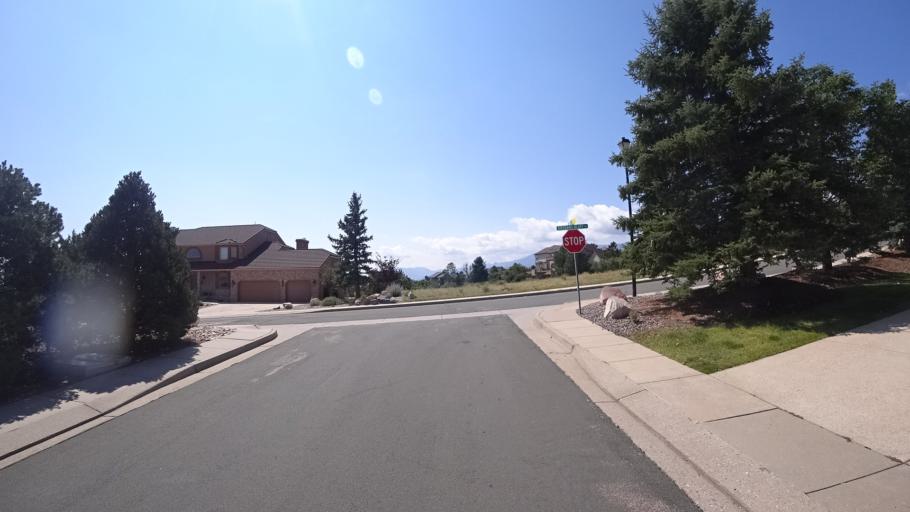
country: US
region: Colorado
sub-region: El Paso County
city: Air Force Academy
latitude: 38.9214
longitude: -104.8741
